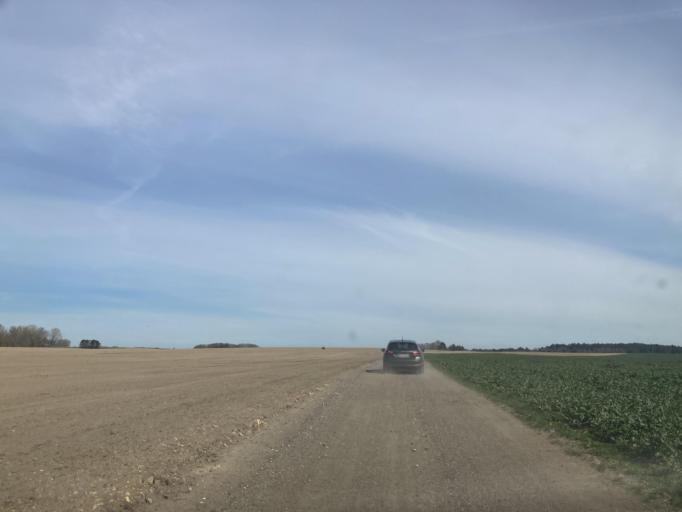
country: DK
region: Capital Region
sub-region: Helsingor Kommune
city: Hornbaek
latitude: 56.0772
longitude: 12.3903
